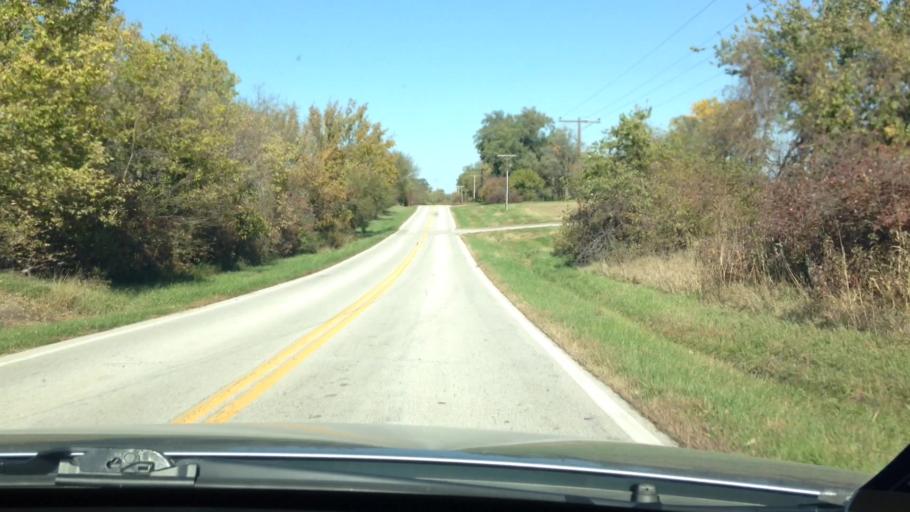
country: US
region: Missouri
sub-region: Clay County
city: Smithville
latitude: 39.3301
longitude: -94.6487
